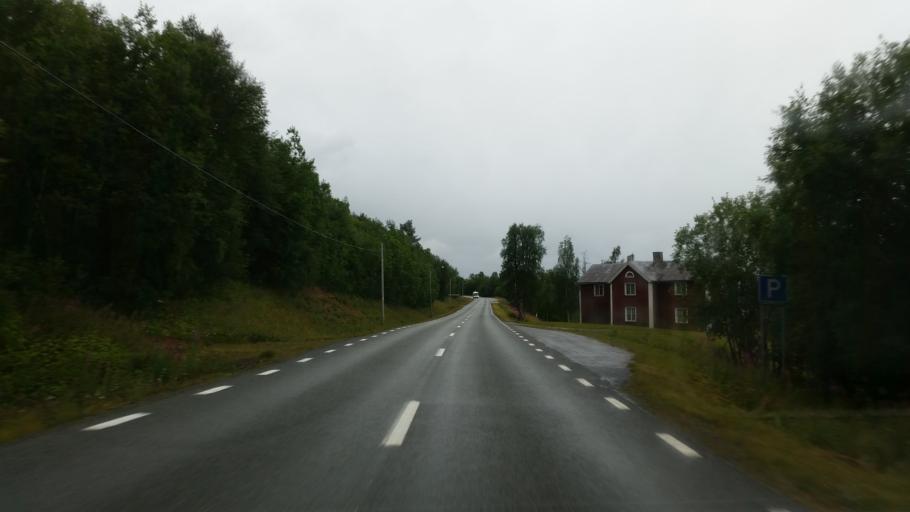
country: NO
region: Nordland
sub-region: Rana
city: Mo i Rana
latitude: 65.8706
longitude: 15.0134
